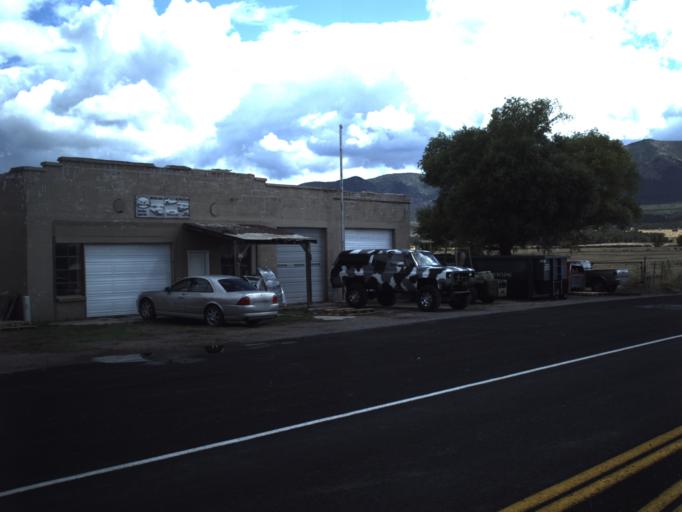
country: US
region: Utah
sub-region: Millard County
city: Fillmore
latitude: 38.7944
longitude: -112.4377
